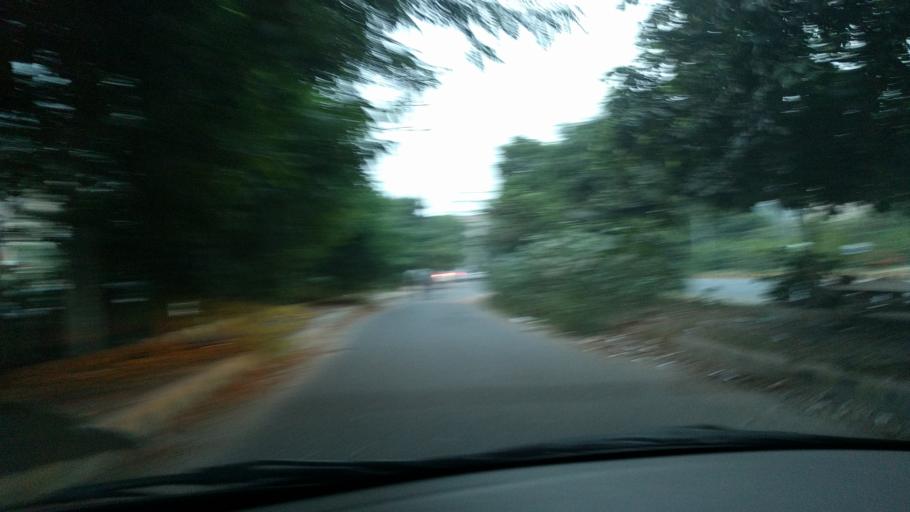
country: IN
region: Haryana
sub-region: Gurgaon
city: Gurgaon
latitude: 28.4533
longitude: 77.0670
